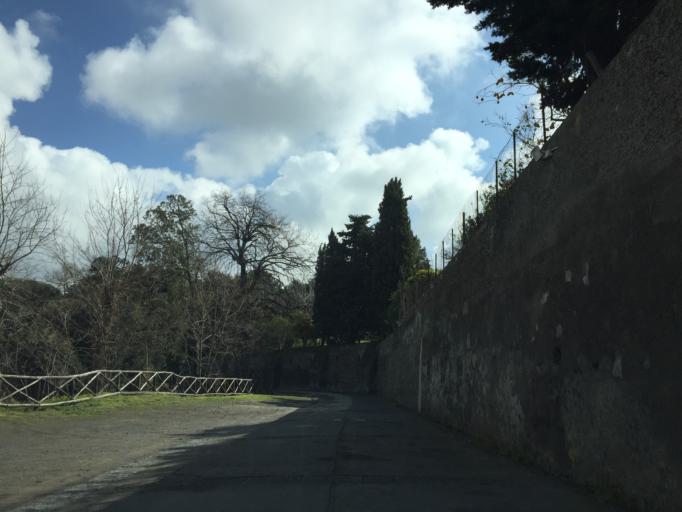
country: IT
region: Campania
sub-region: Provincia di Napoli
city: Torre del Greco
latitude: 40.7808
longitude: 14.4046
